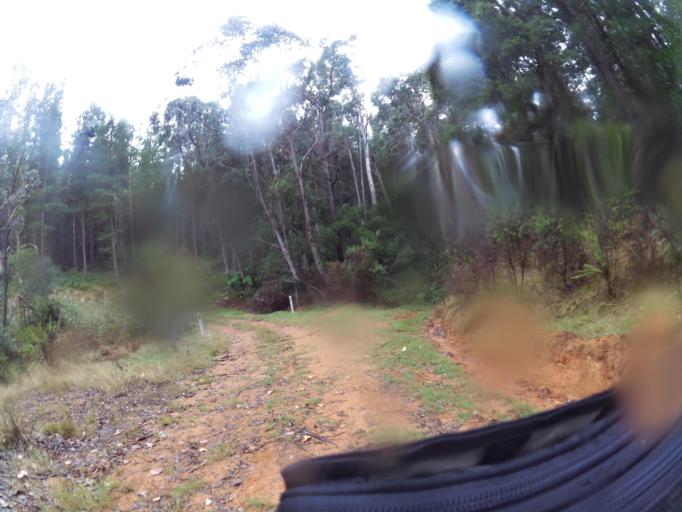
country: AU
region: New South Wales
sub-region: Greater Hume Shire
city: Holbrook
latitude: -36.1981
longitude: 147.5543
